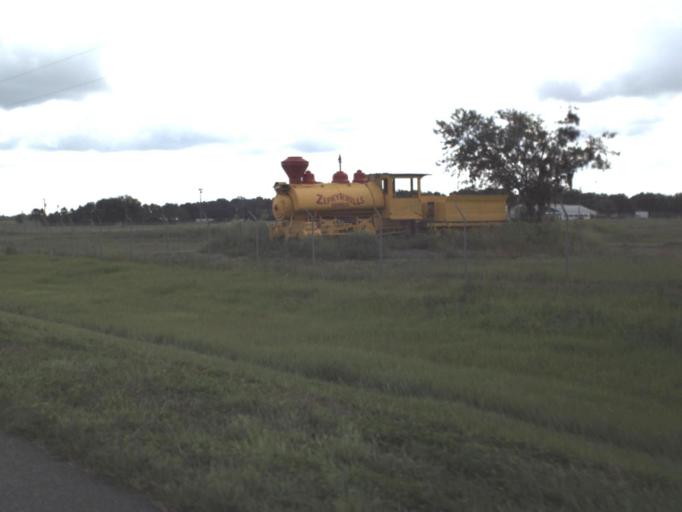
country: US
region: Florida
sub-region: Pasco County
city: Zephyrhills South
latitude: 28.1942
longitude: -82.1994
